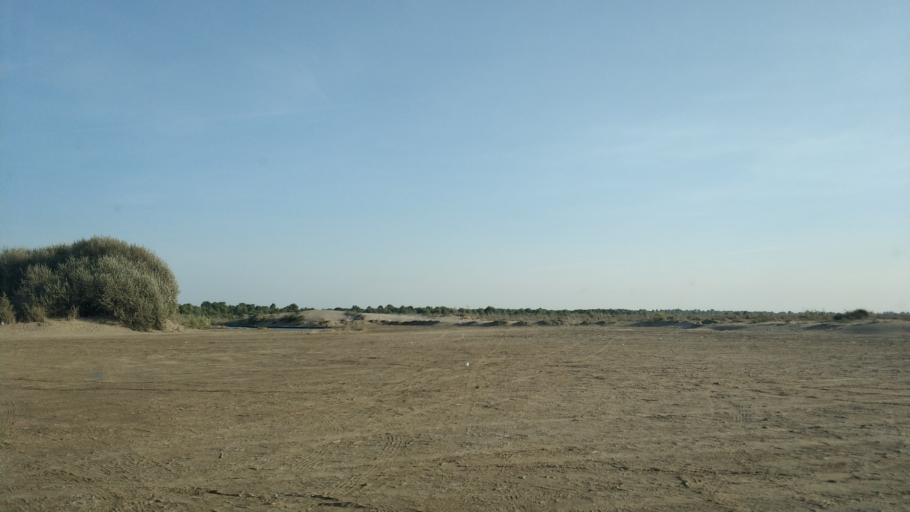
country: AL
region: Fier
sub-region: Rrethi i Lushnjes
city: Divjake
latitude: 40.9578
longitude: 19.4677
